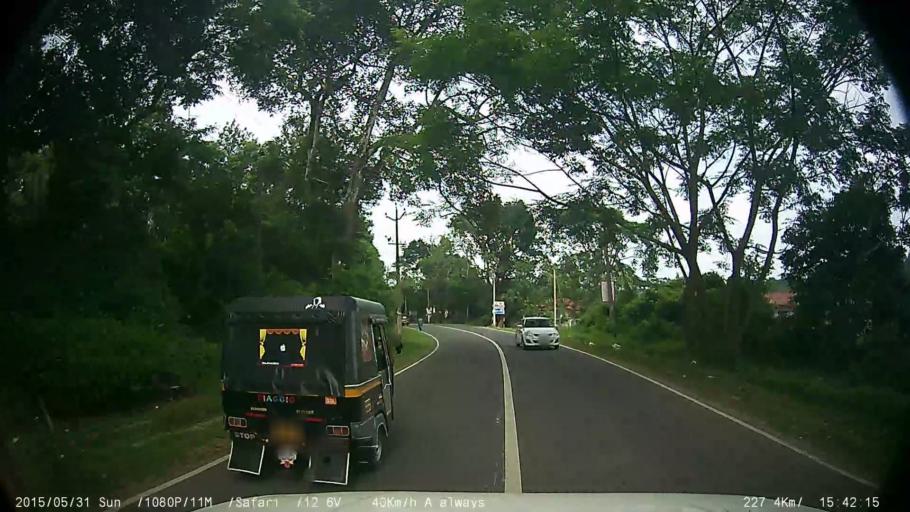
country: IN
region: Kerala
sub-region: Wayanad
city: Panamaram
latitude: 11.6672
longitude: 76.2731
